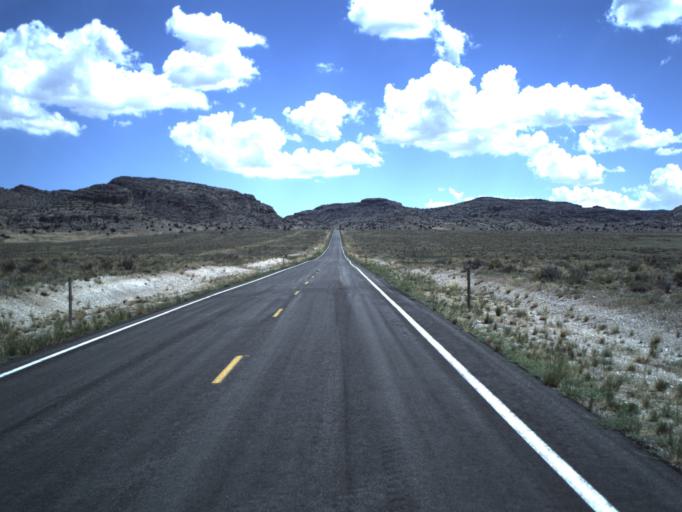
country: US
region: Utah
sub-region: Beaver County
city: Milford
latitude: 39.0757
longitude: -113.6805
